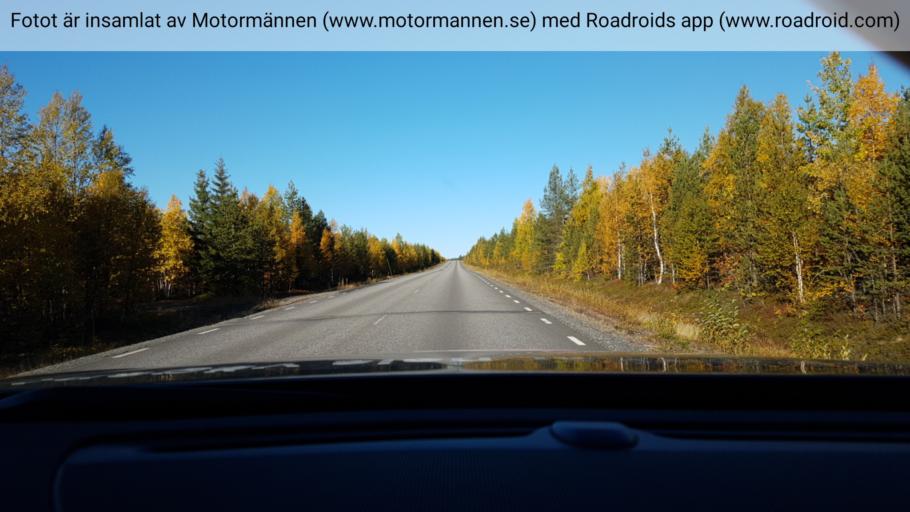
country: SE
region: Vaesterbotten
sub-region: Skelleftea Kommun
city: Storvik
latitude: 65.3258
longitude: 20.6898
